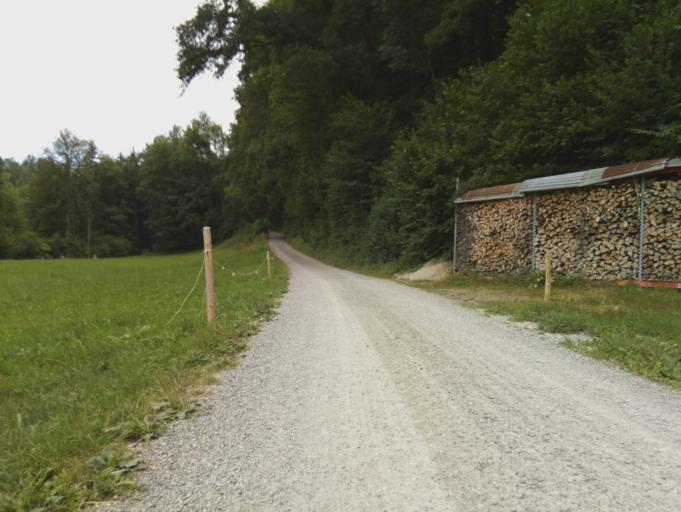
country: CH
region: Saint Gallen
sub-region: Wahlkreis Wil
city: Jonschwil
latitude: 47.4139
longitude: 9.0782
